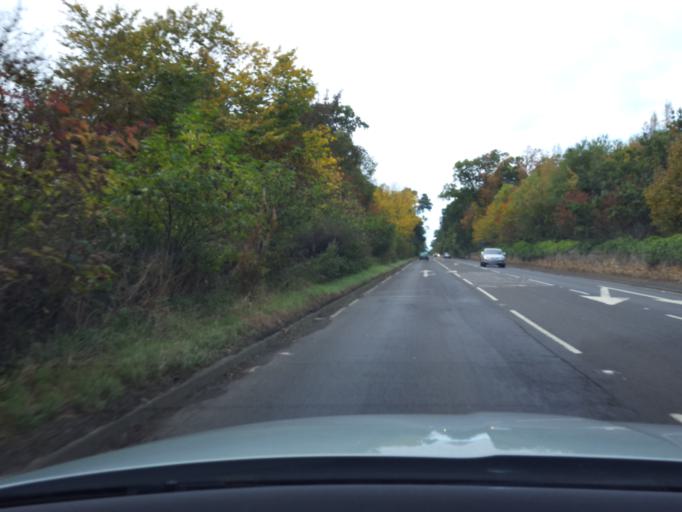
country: GB
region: Scotland
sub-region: Fife
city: Pathhead
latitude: 55.8781
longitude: -2.9862
